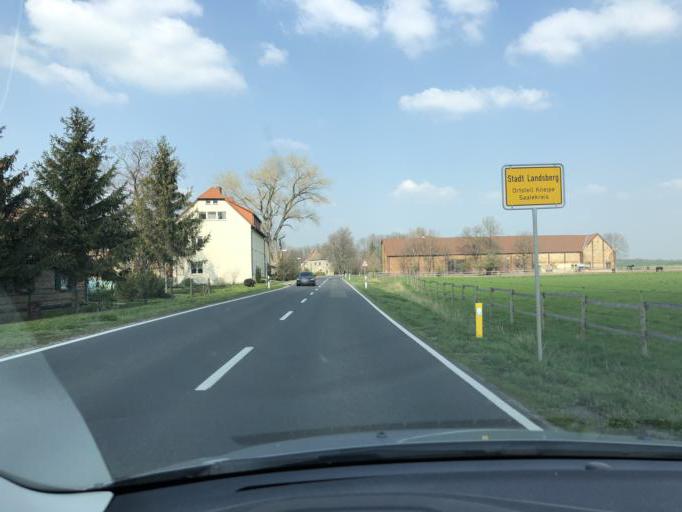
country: DE
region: Saxony-Anhalt
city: Landsberg
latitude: 51.5710
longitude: 12.1437
